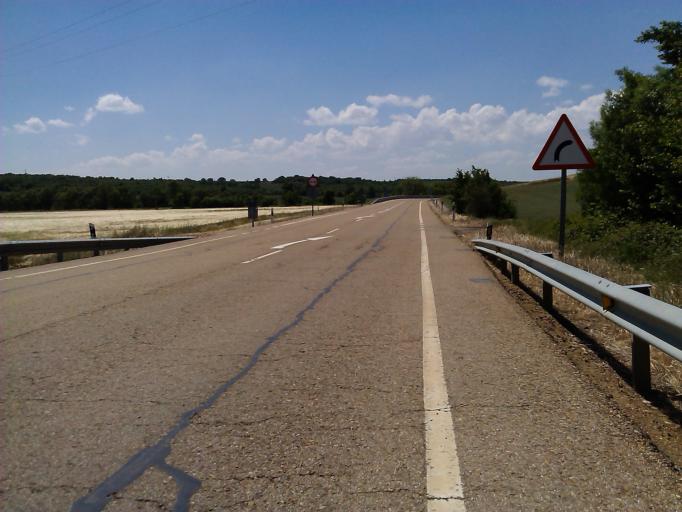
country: ES
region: Castille and Leon
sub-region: Provincia de Palencia
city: Cervatos de la Cueza
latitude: 42.3295
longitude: -4.8102
